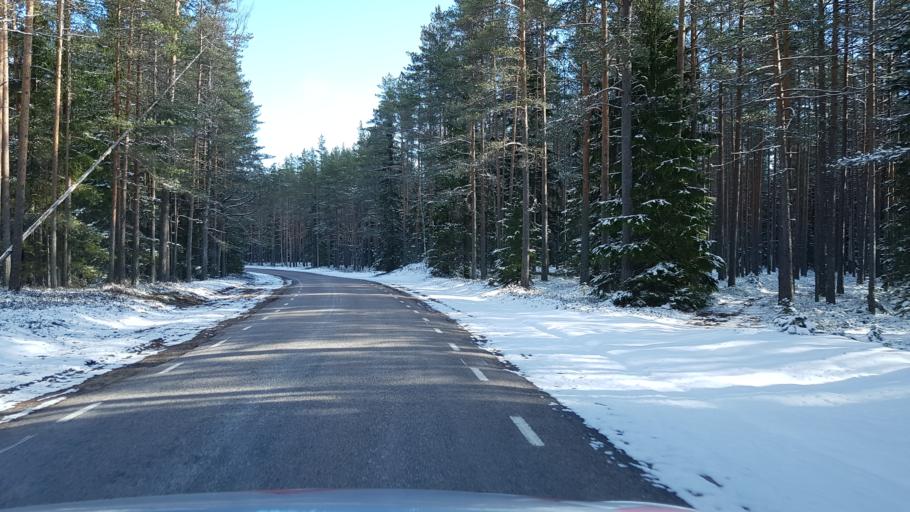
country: EE
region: Harju
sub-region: Loksa linn
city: Loksa
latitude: 59.5357
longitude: 25.9773
